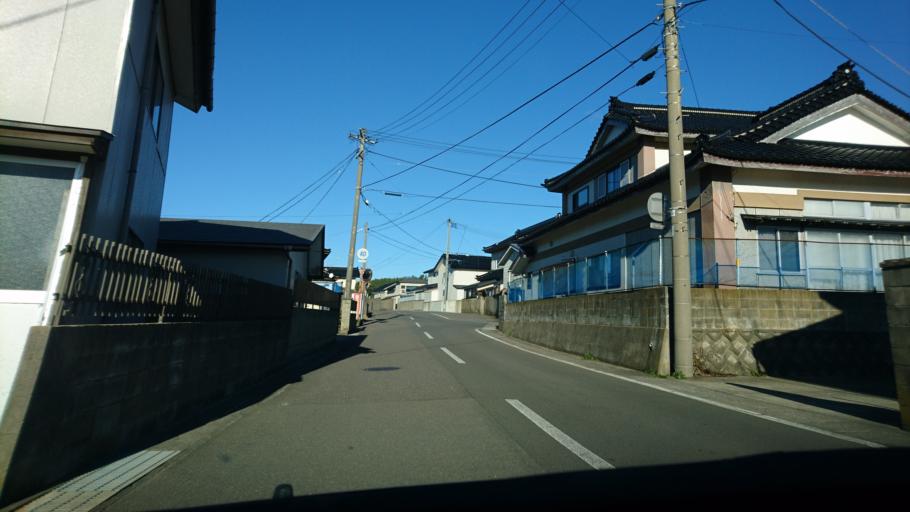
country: JP
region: Yamagata
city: Yuza
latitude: 39.3671
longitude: 140.0115
